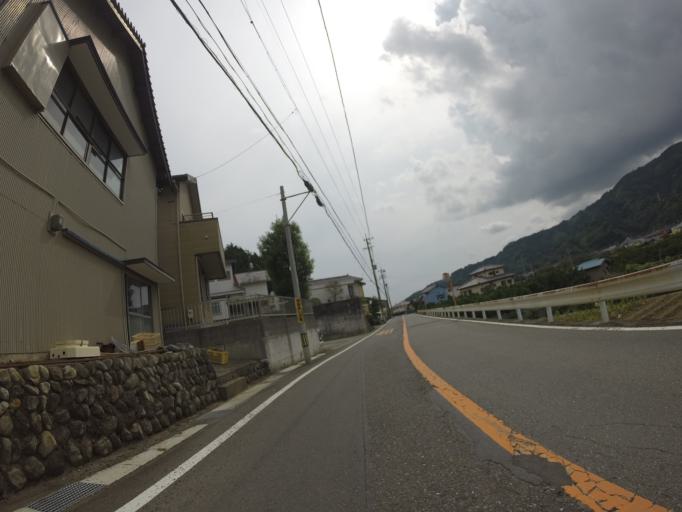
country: JP
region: Shizuoka
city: Fujinomiya
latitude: 35.0705
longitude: 138.5273
